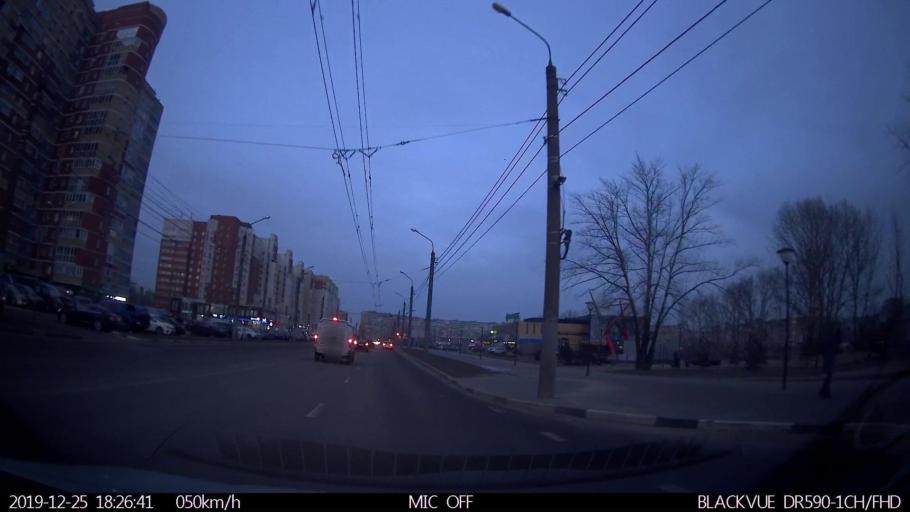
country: RU
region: Nizjnij Novgorod
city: Nizhniy Novgorod
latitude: 56.3379
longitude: 43.9371
